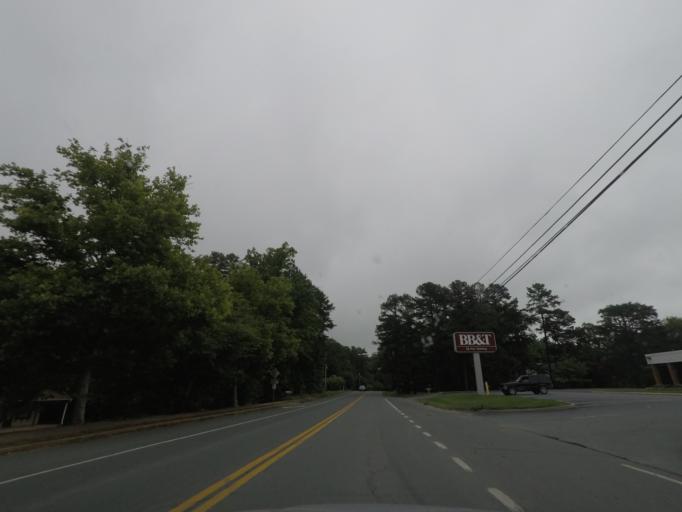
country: US
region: Virginia
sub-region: Fluvanna County
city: Weber City
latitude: 37.7581
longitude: -78.2673
